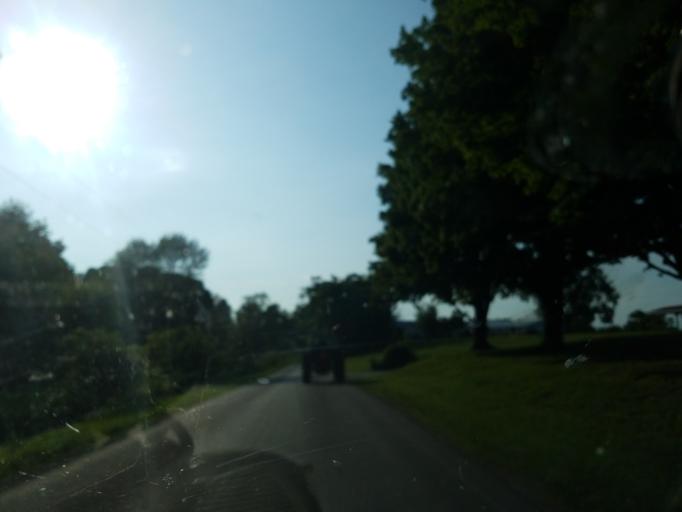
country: US
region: Ohio
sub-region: Adams County
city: West Union
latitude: 38.8909
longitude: -83.5163
